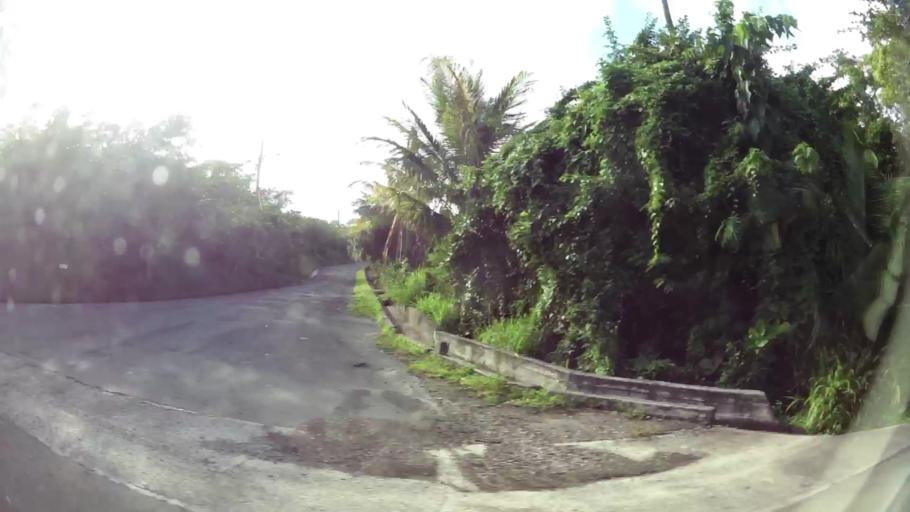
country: AG
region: Saint Peter
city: All Saints
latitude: 17.0483
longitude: -61.8120
